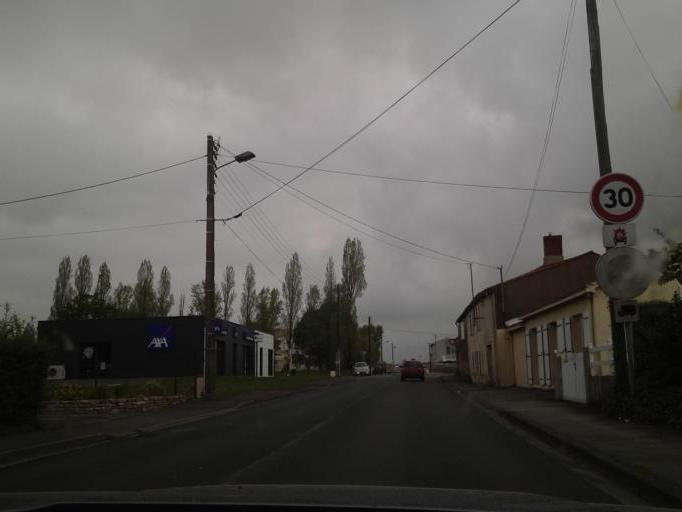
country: FR
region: Pays de la Loire
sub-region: Departement de la Vendee
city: Fontenay-le-Comte
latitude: 46.4531
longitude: -0.8057
